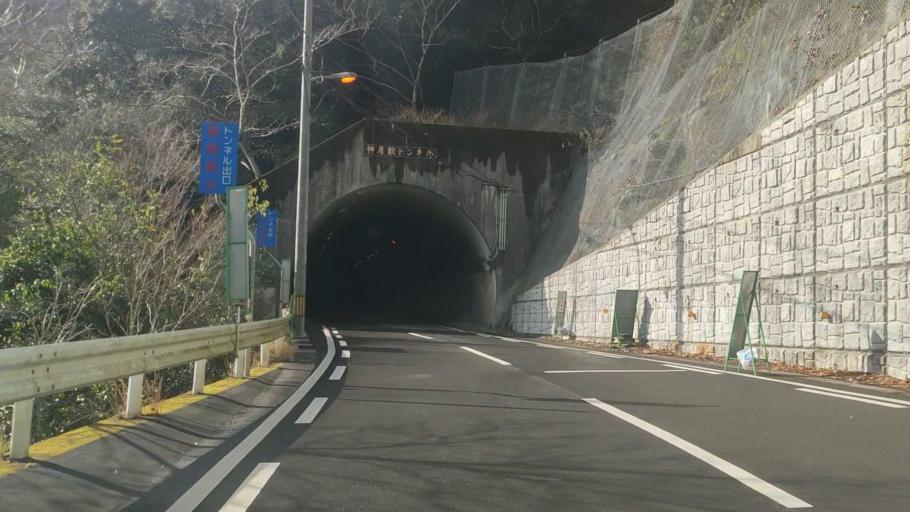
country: JP
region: Kumamoto
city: Hitoyoshi
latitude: 32.4173
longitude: 130.8454
